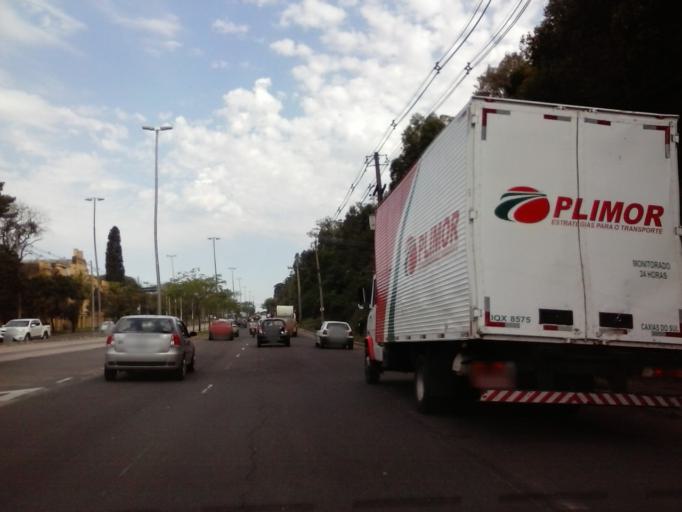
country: BR
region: Rio Grande do Sul
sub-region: Porto Alegre
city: Porto Alegre
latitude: -30.0700
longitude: -51.1422
